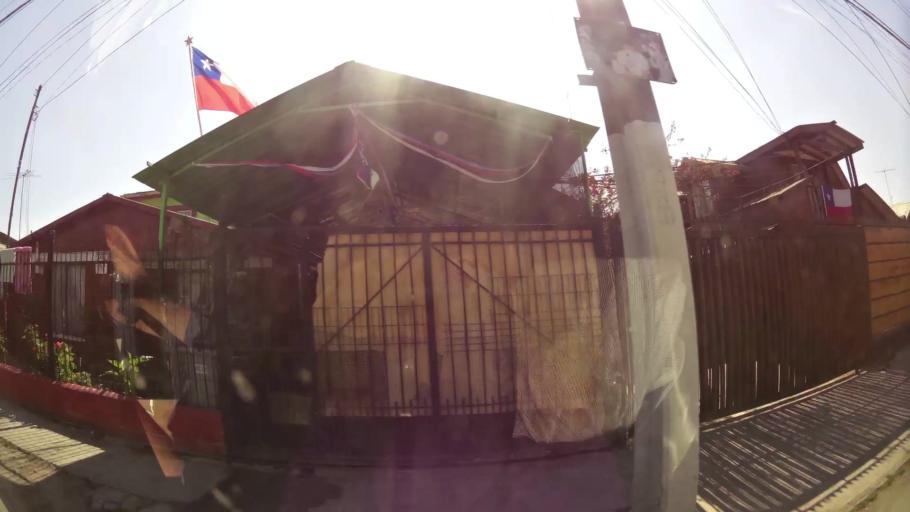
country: CL
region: Santiago Metropolitan
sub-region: Provincia de Talagante
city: Penaflor
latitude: -33.5677
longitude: -70.7991
